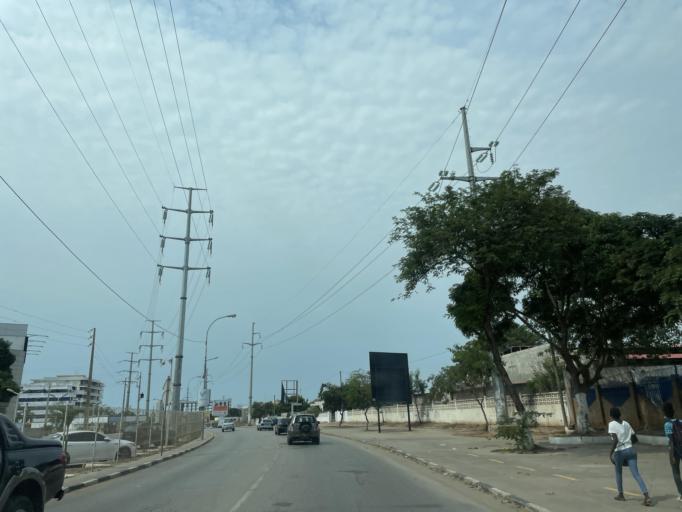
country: AO
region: Luanda
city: Luanda
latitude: -8.9102
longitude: 13.2002
